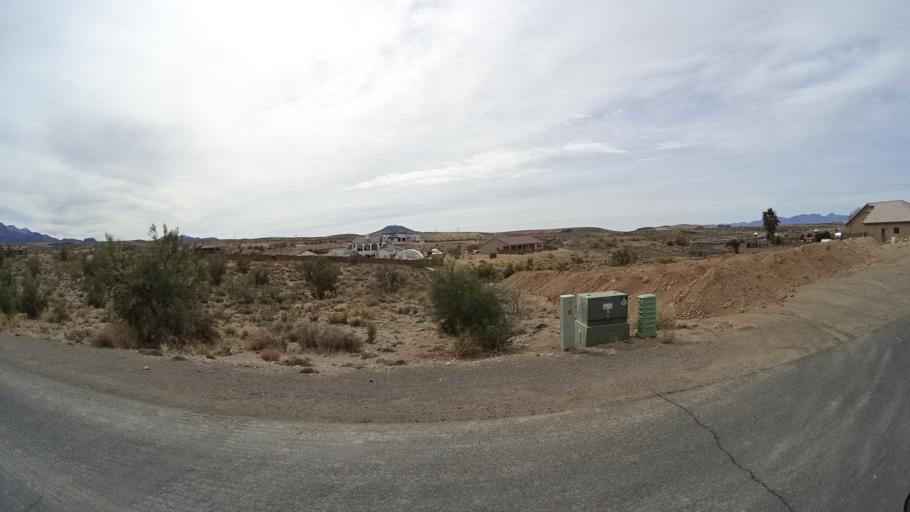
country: US
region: Arizona
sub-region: Mohave County
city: Kingman
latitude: 35.1784
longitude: -113.9982
